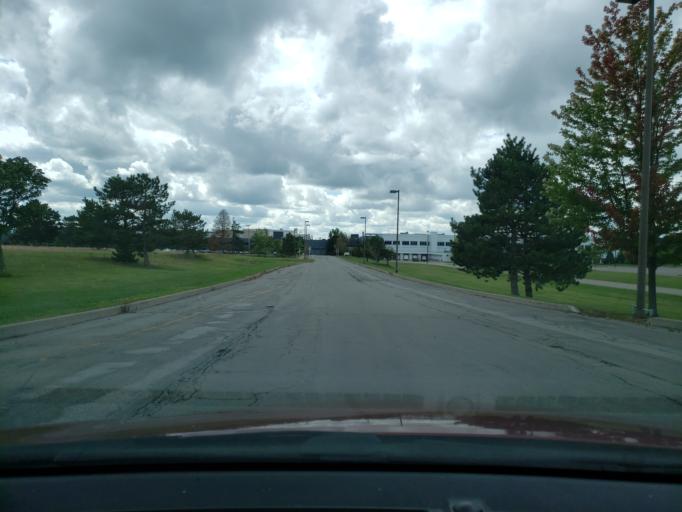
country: US
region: New York
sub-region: Monroe County
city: North Gates
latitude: 43.1566
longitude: -77.7463
